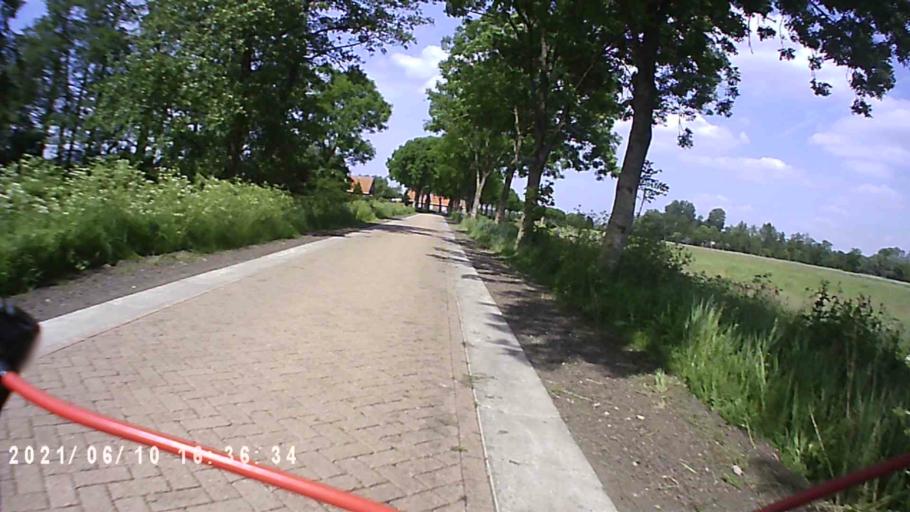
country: NL
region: Friesland
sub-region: Gemeente Achtkarspelen
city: Buitenpost
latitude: 53.2377
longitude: 6.1394
